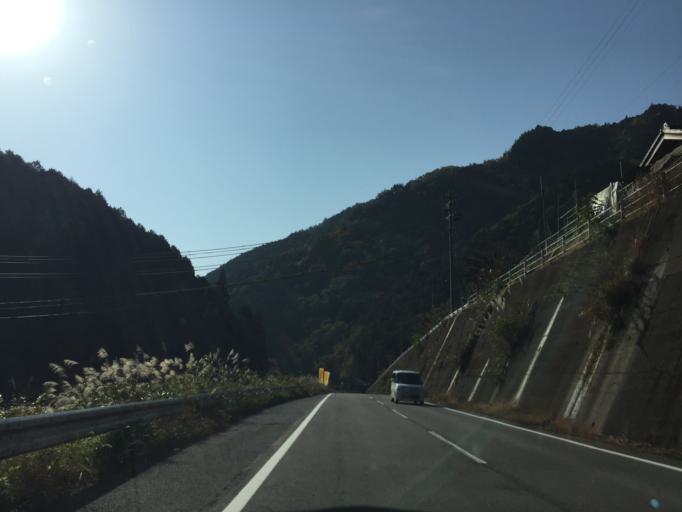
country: JP
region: Gifu
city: Minokamo
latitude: 35.5548
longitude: 137.1154
